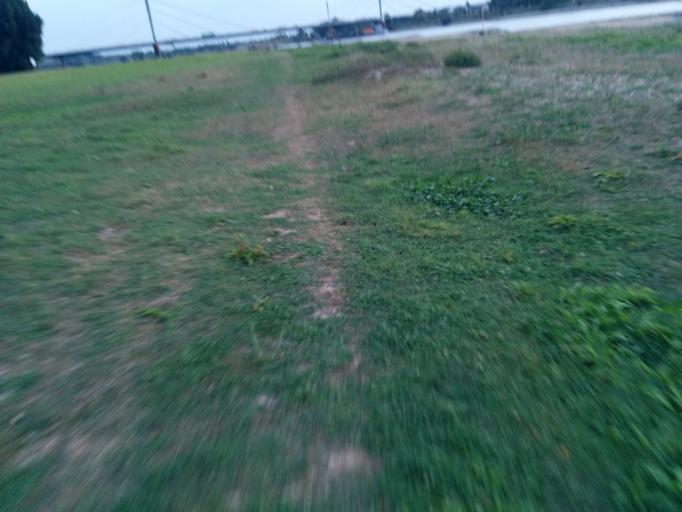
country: DE
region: North Rhine-Westphalia
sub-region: Regierungsbezirk Dusseldorf
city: Hochfeld
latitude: 51.4444
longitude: 6.7163
